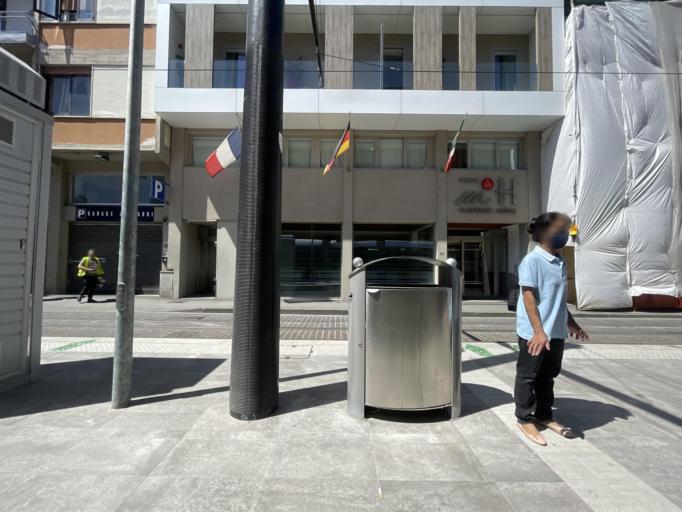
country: IT
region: Tuscany
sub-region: Province of Florence
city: Florence
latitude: 43.7787
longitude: 11.2450
